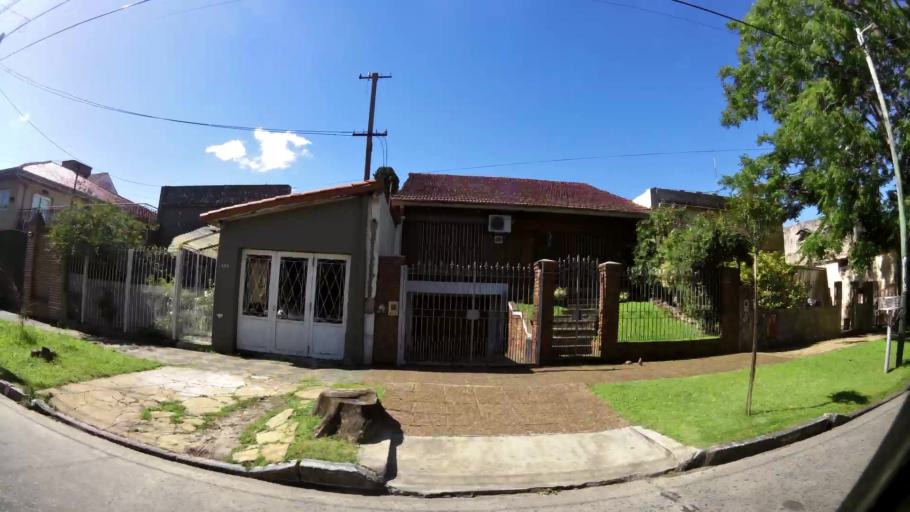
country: AR
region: Buenos Aires
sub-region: Partido de Lomas de Zamora
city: Lomas de Zamora
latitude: -34.7609
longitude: -58.4153
